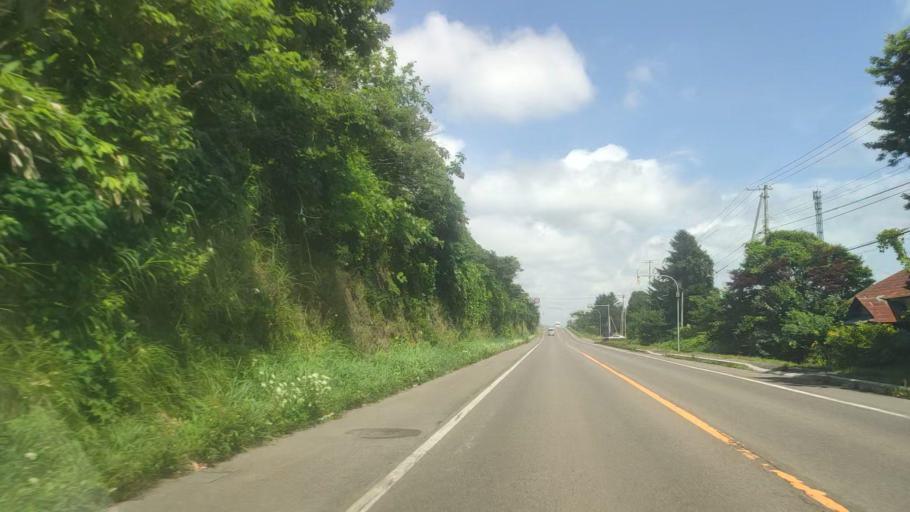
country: JP
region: Hokkaido
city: Niseko Town
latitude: 42.3607
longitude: 140.2870
